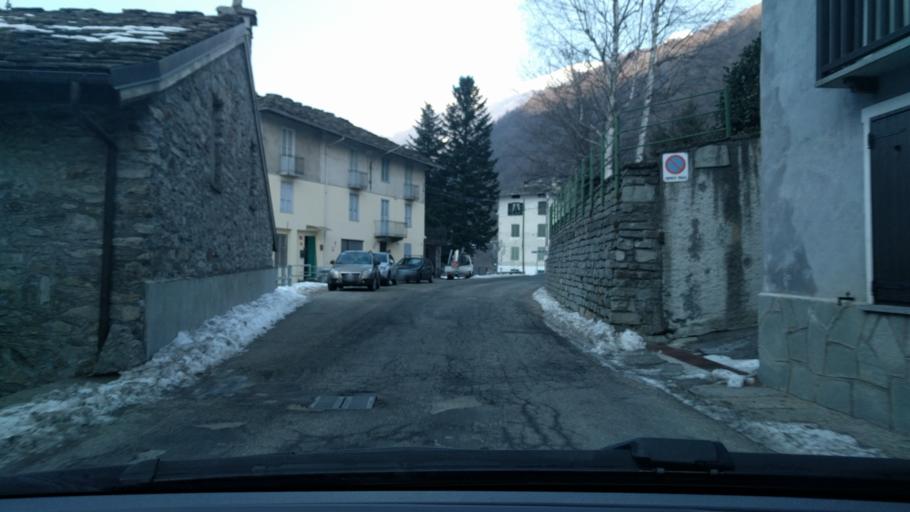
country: IT
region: Piedmont
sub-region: Provincia di Torino
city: Chialamberto
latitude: 45.3681
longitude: 7.3051
